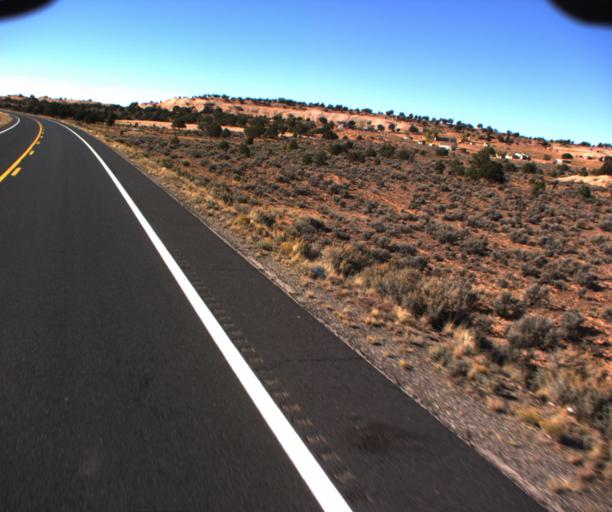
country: US
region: Arizona
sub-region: Coconino County
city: Kaibito
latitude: 36.5609
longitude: -110.7218
